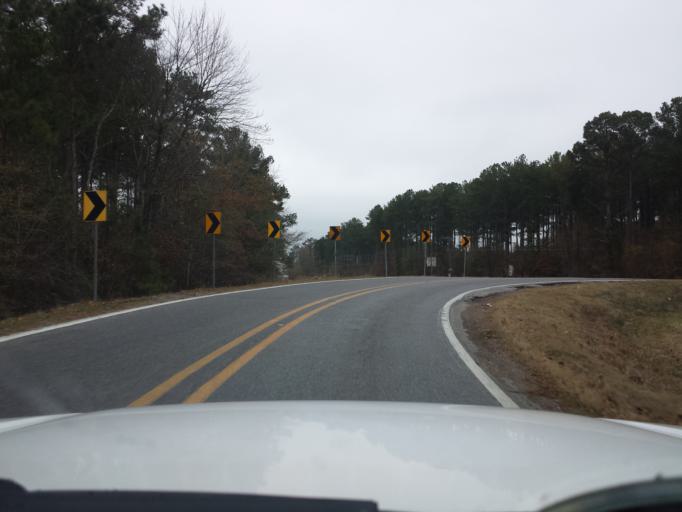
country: US
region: Mississippi
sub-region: Madison County
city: Canton
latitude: 32.4987
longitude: -89.9259
